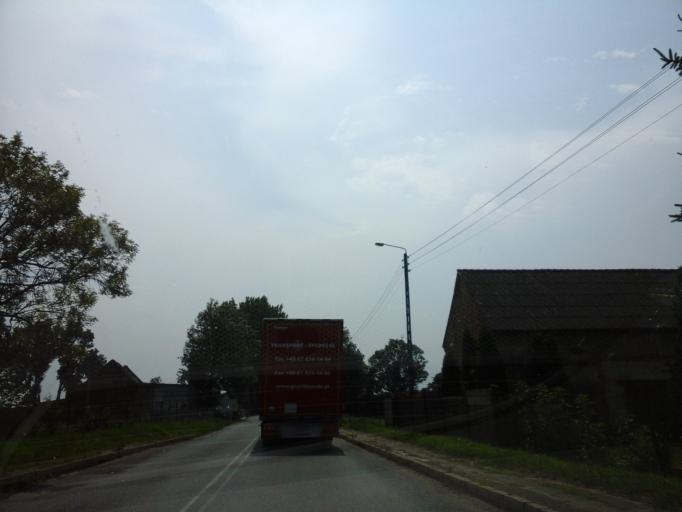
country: PL
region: Lower Silesian Voivodeship
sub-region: Powiat wroclawski
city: Zorawina
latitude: 50.9113
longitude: 17.0652
